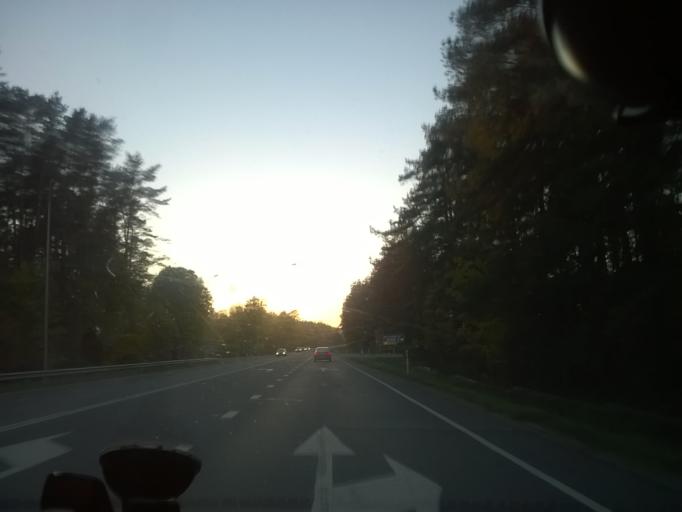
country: EE
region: Laeaene
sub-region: Lihula vald
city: Lihula
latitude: 58.9716
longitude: 23.8890
